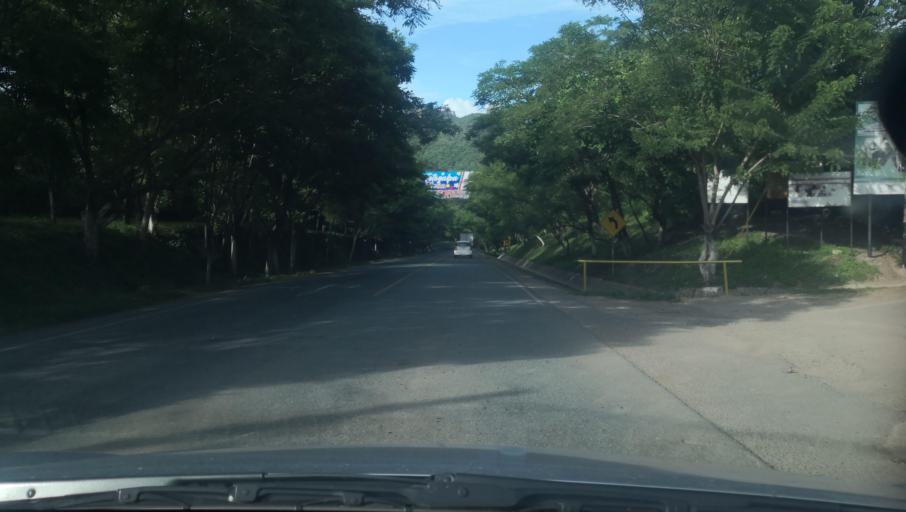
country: NI
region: Madriz
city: Totogalpa
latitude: 13.5627
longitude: -86.4885
